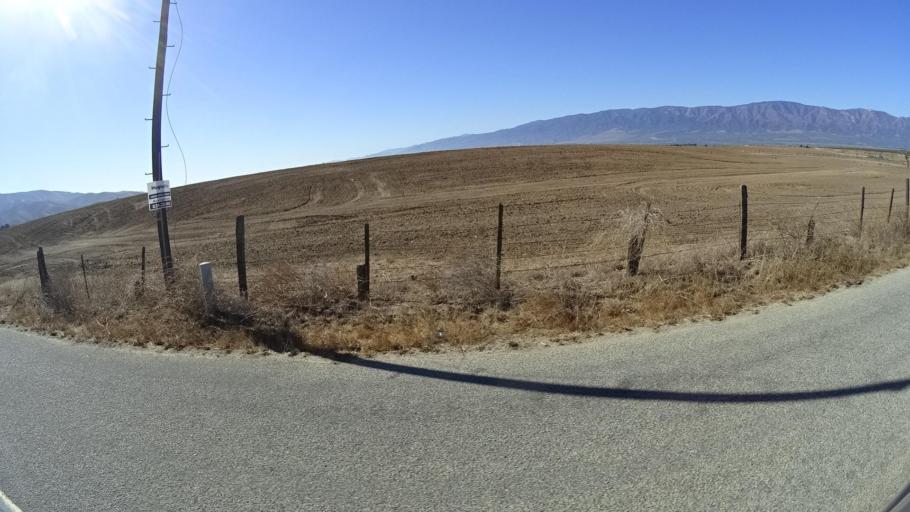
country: US
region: California
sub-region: Monterey County
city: Gonzales
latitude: 36.5114
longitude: -121.3627
